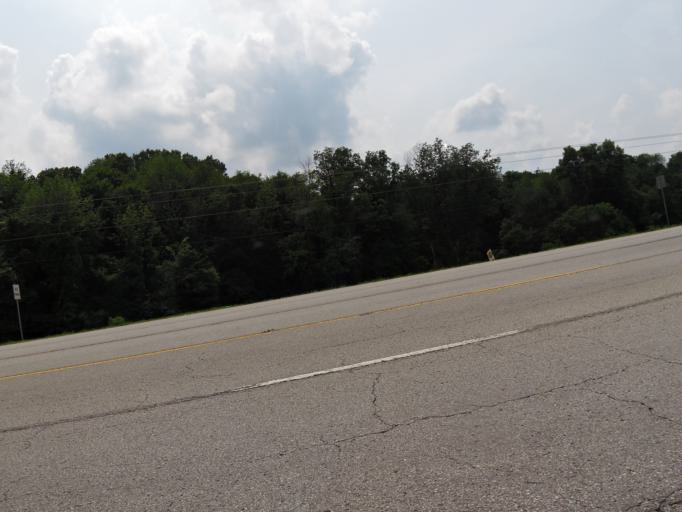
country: US
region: Kentucky
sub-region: Gallatin County
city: Warsaw
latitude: 38.6954
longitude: -84.9413
